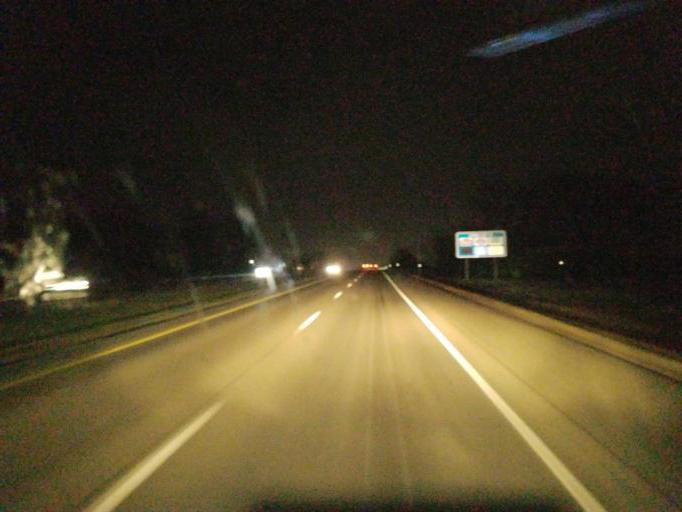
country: US
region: Iowa
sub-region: Dallas County
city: Waukee
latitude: 41.5768
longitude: -93.8385
